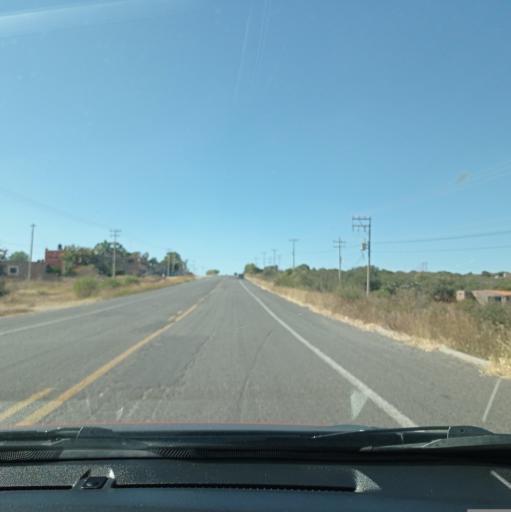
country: MX
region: Jalisco
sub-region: San Julian
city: Colonia Veintitres de Mayo
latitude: 21.0087
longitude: -102.2976
